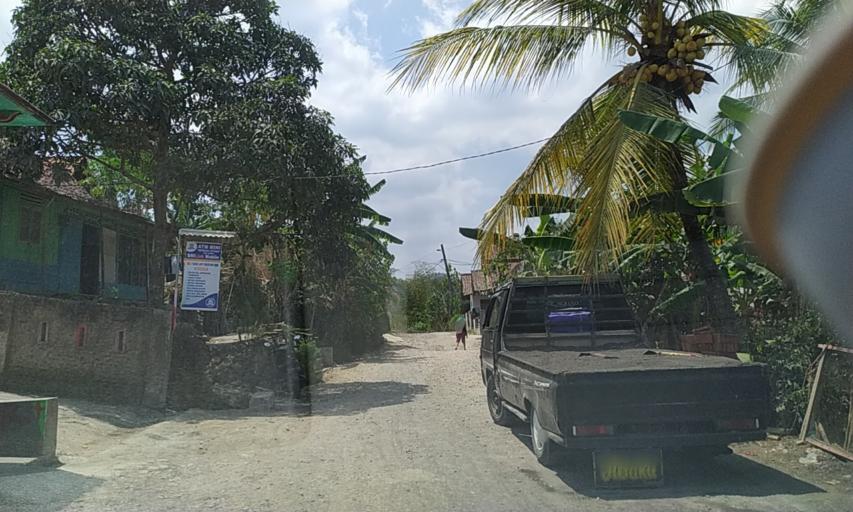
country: ID
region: Central Java
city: Karanggintung
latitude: -7.4781
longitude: 108.9095
